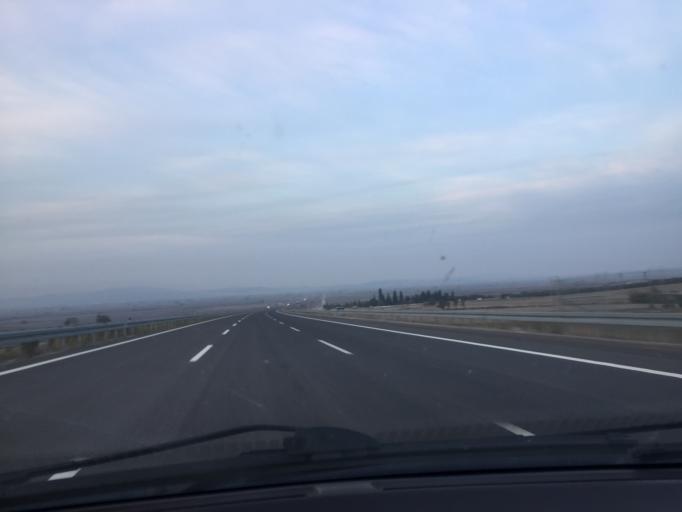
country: TR
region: Manisa
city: Halitpasa
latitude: 38.6990
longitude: 27.6430
